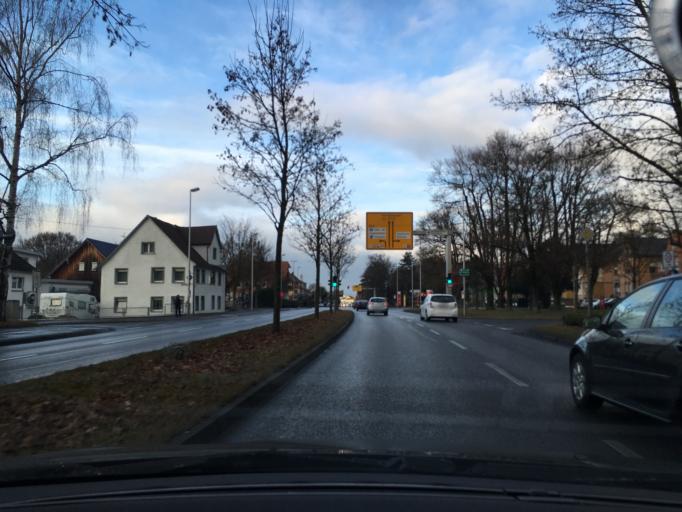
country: DE
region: Baden-Wuerttemberg
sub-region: Tuebingen Region
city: Weingarten
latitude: 47.8075
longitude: 9.6372
